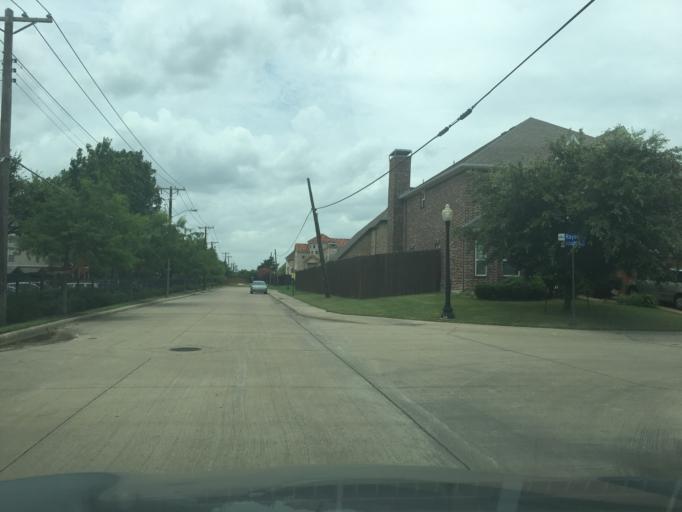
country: US
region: Texas
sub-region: Dallas County
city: Richardson
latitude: 32.9365
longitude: -96.7267
